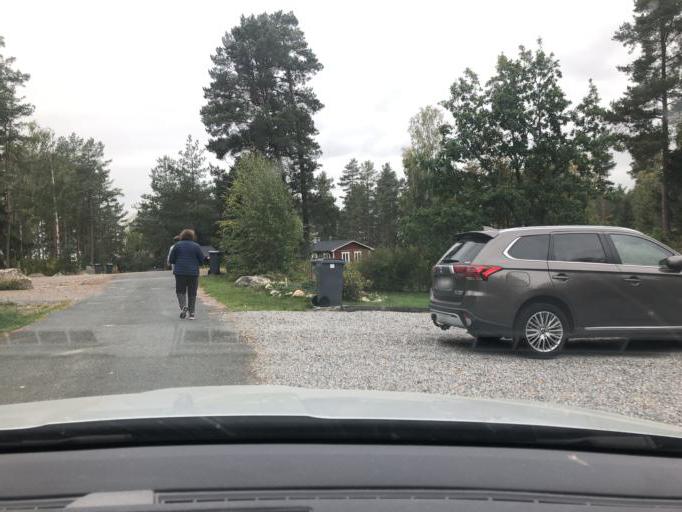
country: SE
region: Vaestmanland
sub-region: Kungsors Kommun
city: Kungsoer
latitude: 59.2285
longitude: 16.0811
